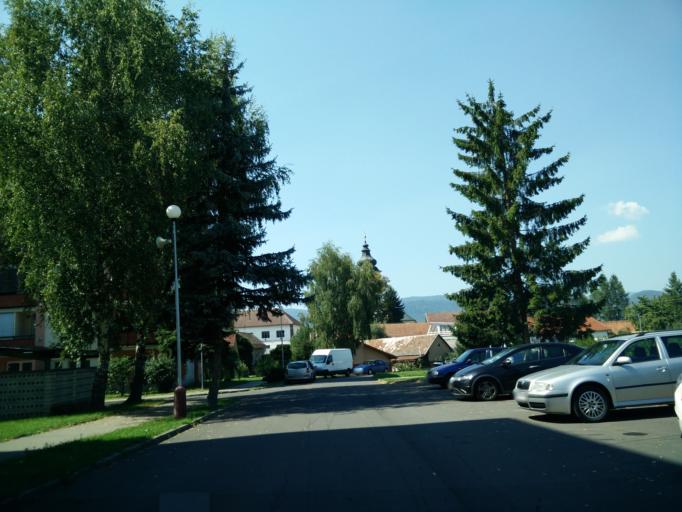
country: SK
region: Banskobystricky
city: Ziar nad Hronom
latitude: 48.5409
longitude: 18.7836
